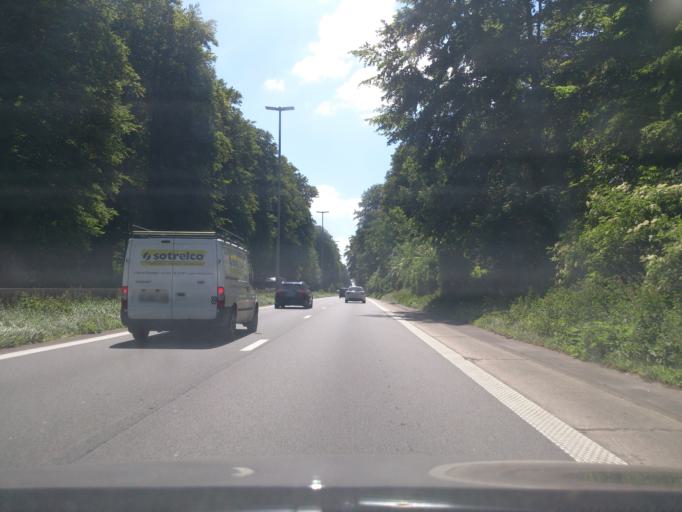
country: BE
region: Flanders
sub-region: Provincie Vlaams-Brabant
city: Hoeilaart
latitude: 50.7554
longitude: 4.4354
